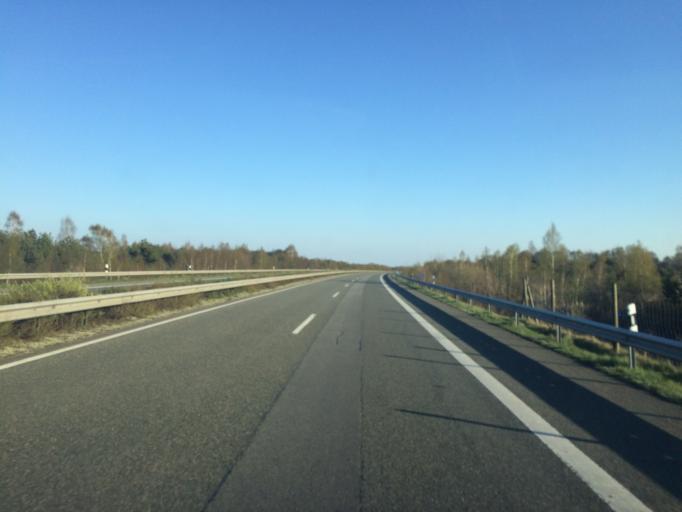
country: DE
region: Lower Saxony
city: Geeste
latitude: 52.6541
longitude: 7.1896
